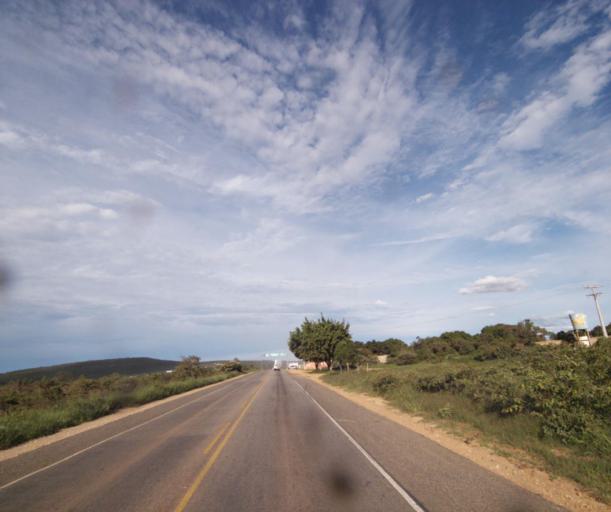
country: BR
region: Bahia
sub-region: Caetite
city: Caetite
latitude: -14.0671
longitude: -42.5296
